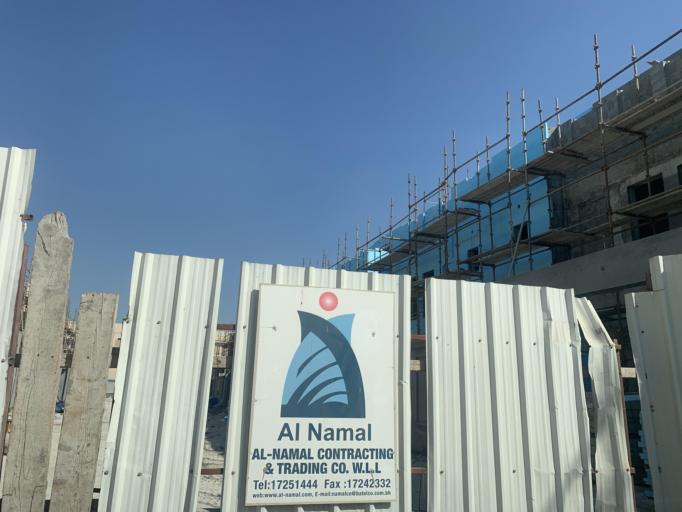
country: BH
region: Central Governorate
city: Madinat Hamad
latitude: 26.1209
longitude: 50.4812
